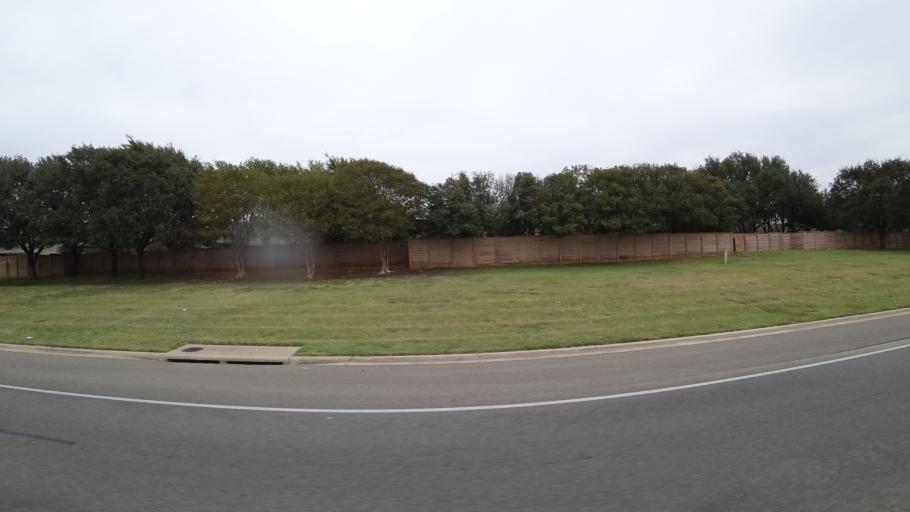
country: US
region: Texas
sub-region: Williamson County
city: Brushy Creek
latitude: 30.4912
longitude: -97.7726
